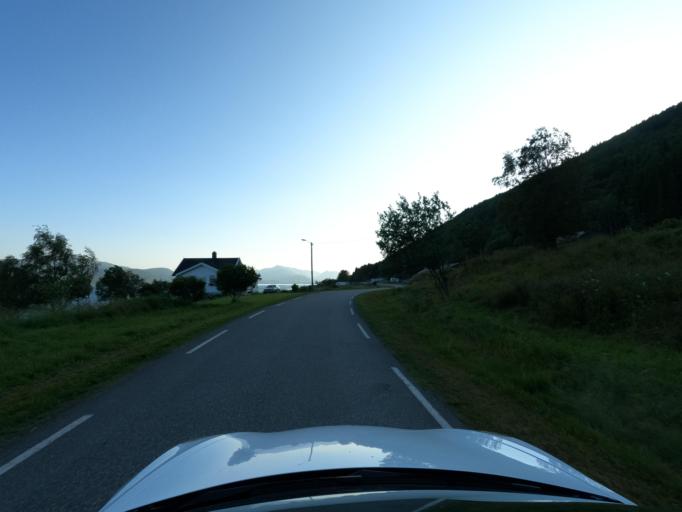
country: NO
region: Nordland
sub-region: Ballangen
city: Ballangen
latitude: 68.4649
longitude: 16.7786
